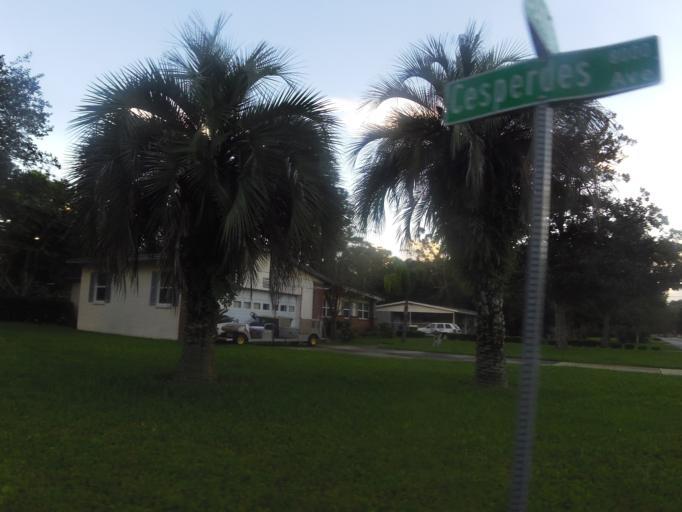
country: US
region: Florida
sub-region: Duval County
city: Jacksonville
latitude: 30.2346
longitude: -81.6156
